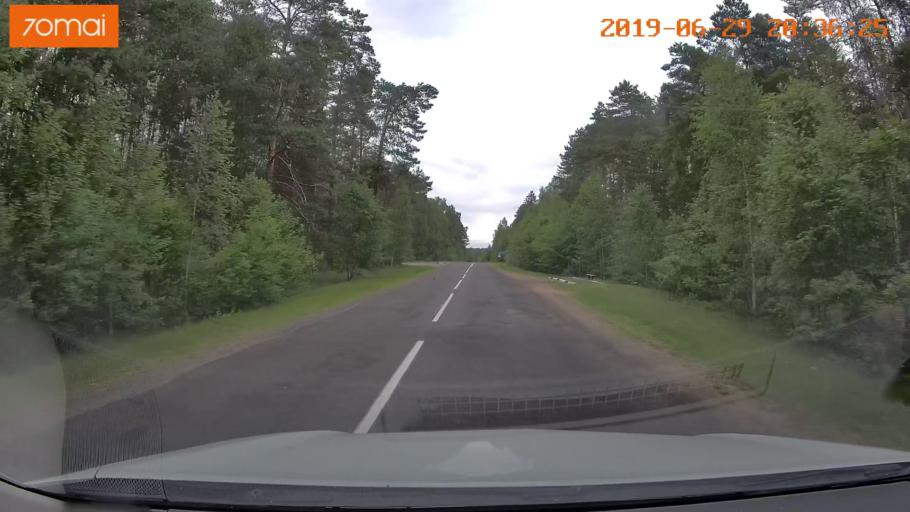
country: BY
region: Brest
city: Hantsavichy
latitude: 52.5260
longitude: 26.3583
